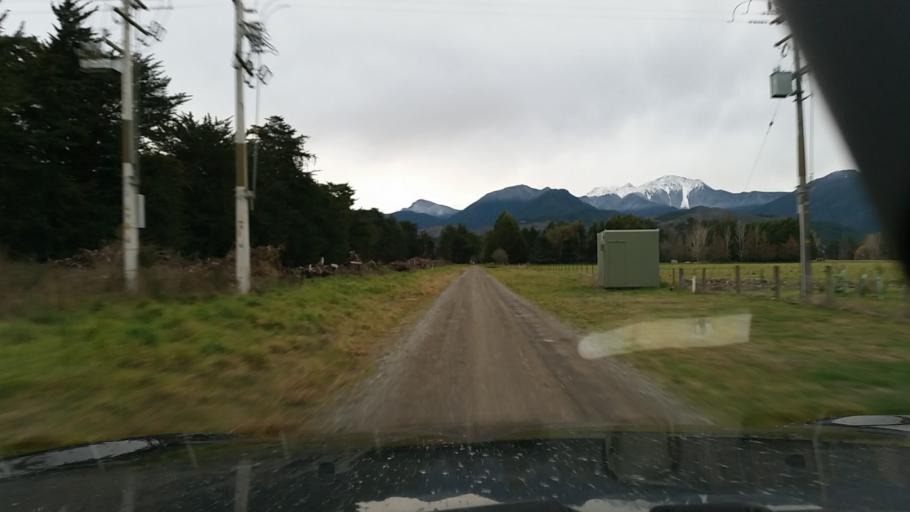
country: NZ
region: Nelson
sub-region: Nelson City
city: Nelson
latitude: -41.5659
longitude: 173.5247
